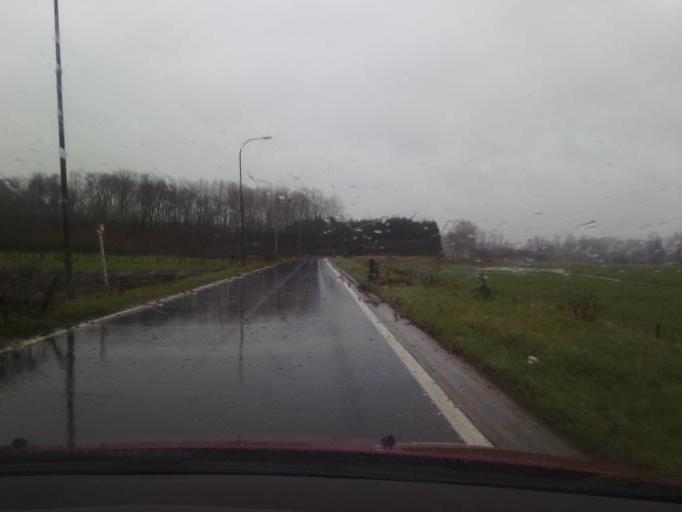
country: BE
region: Flanders
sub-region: Provincie Oost-Vlaanderen
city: Wichelen
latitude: 51.0224
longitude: 3.9729
